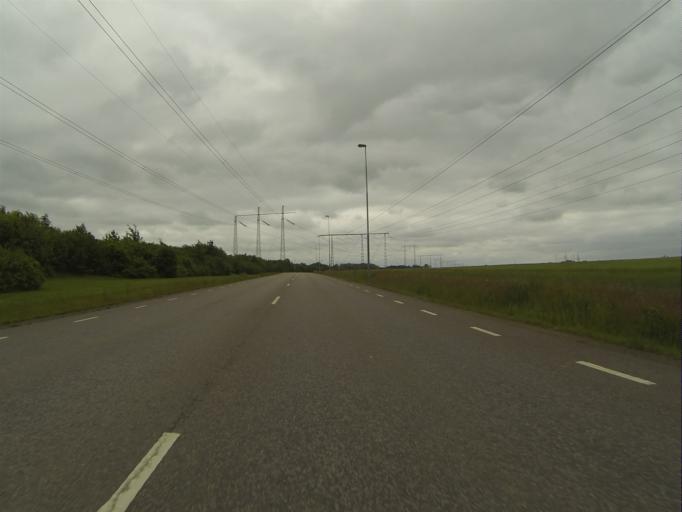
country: SE
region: Skane
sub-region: Staffanstorps Kommun
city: Staffanstorp
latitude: 55.6508
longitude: 13.1996
